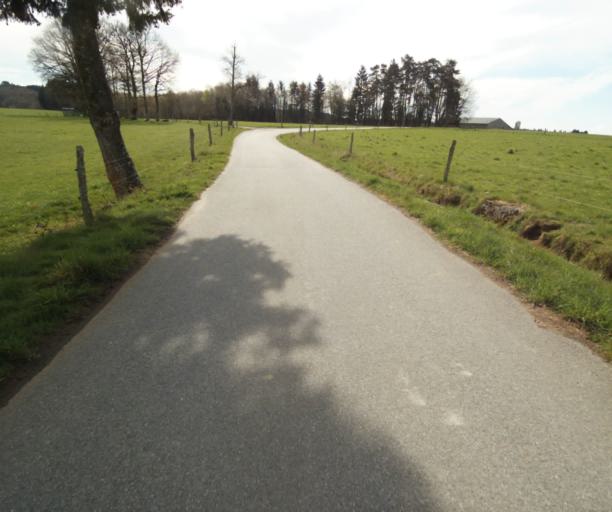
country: FR
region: Limousin
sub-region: Departement de la Correze
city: Correze
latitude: 45.3592
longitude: 1.8853
